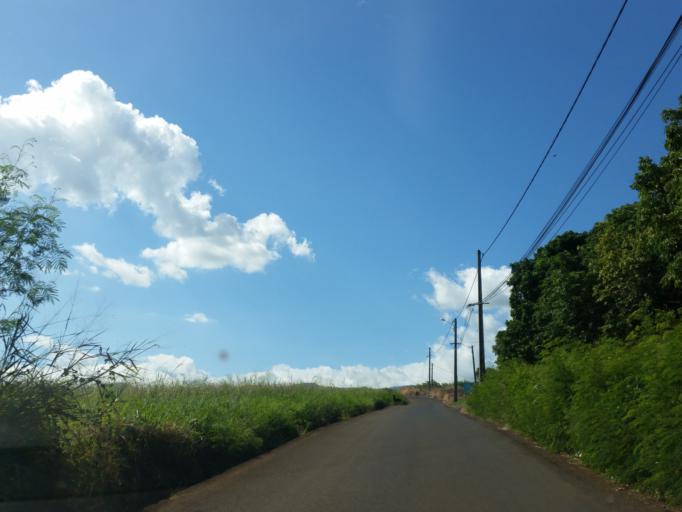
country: RE
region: Reunion
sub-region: Reunion
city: Saint-Pierre
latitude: -21.3187
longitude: 55.5036
